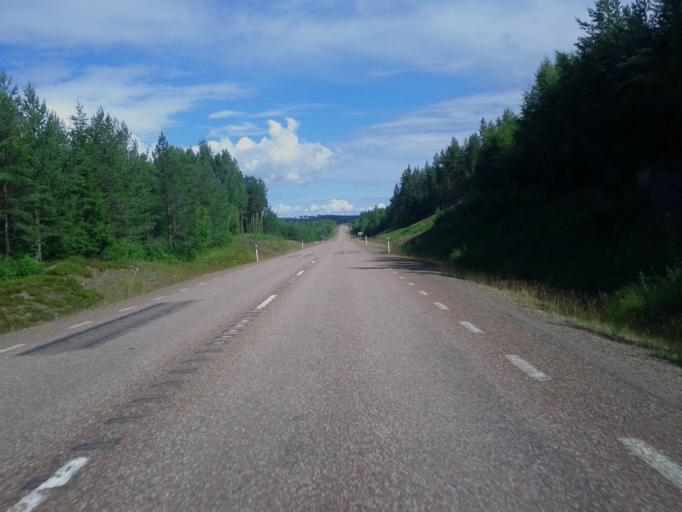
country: SE
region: Dalarna
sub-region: Rattviks Kommun
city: Raettvik
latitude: 60.8430
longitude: 15.1914
